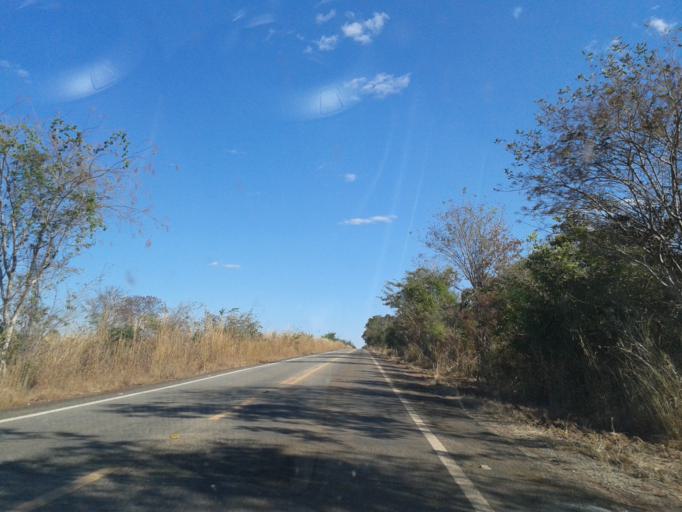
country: BR
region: Goias
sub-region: Mozarlandia
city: Mozarlandia
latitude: -14.5455
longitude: -50.4915
